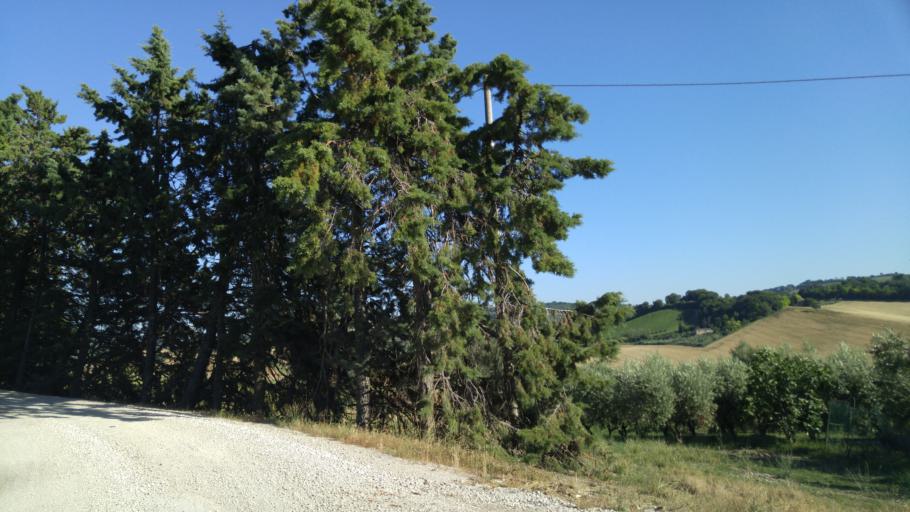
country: IT
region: The Marches
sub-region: Provincia di Pesaro e Urbino
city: Cartoceto
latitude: 43.7906
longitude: 12.8867
